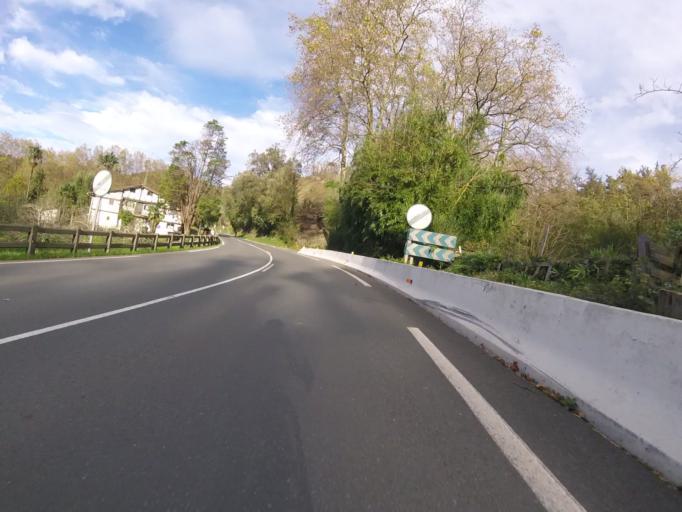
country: ES
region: Basque Country
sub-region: Provincia de Guipuzcoa
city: Usurbil
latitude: 43.2765
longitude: -2.0564
